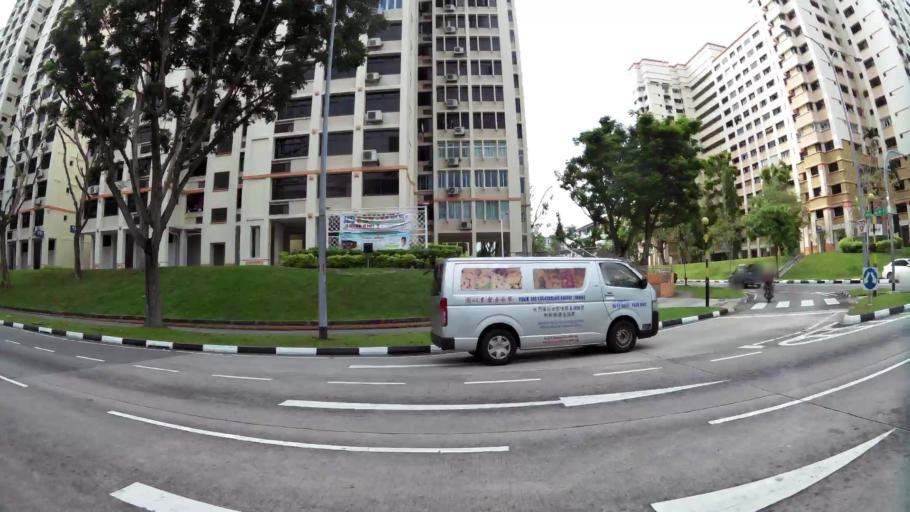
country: SG
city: Singapore
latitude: 1.3770
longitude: 103.8846
